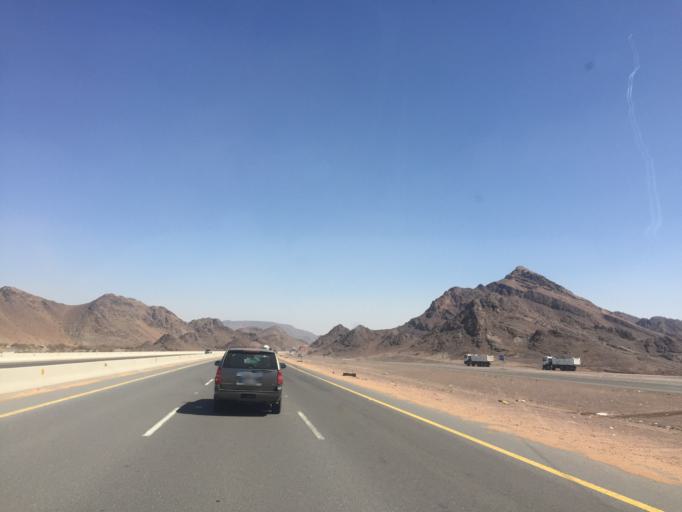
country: SA
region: Al Madinah al Munawwarah
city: Sultanah
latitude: 24.3159
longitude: 39.4276
